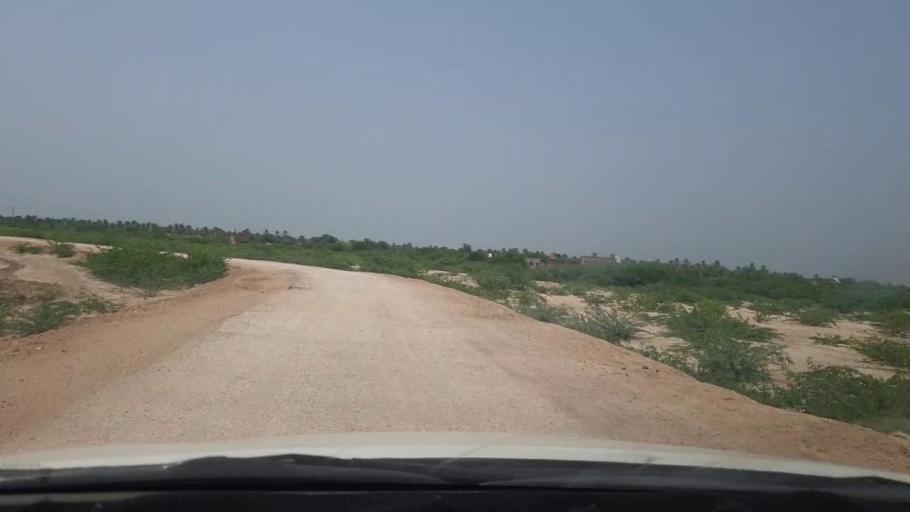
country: PK
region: Sindh
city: Khairpur
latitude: 27.5005
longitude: 68.8863
